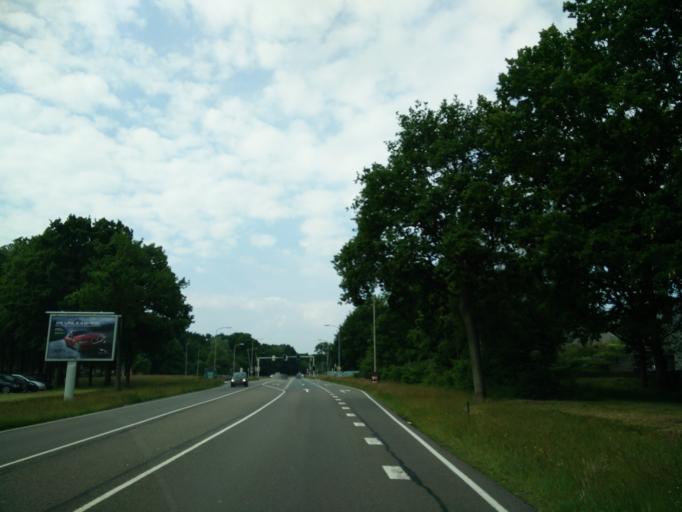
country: NL
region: Drenthe
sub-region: Gemeente Assen
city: Assen
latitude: 53.0093
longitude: 6.5500
